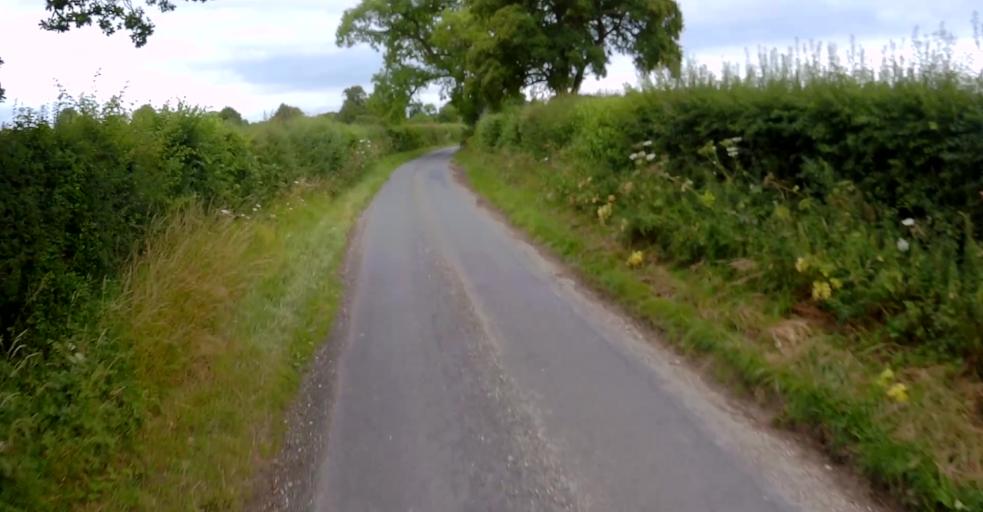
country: GB
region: England
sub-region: Hampshire
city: Kings Worthy
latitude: 51.0679
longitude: -1.2069
